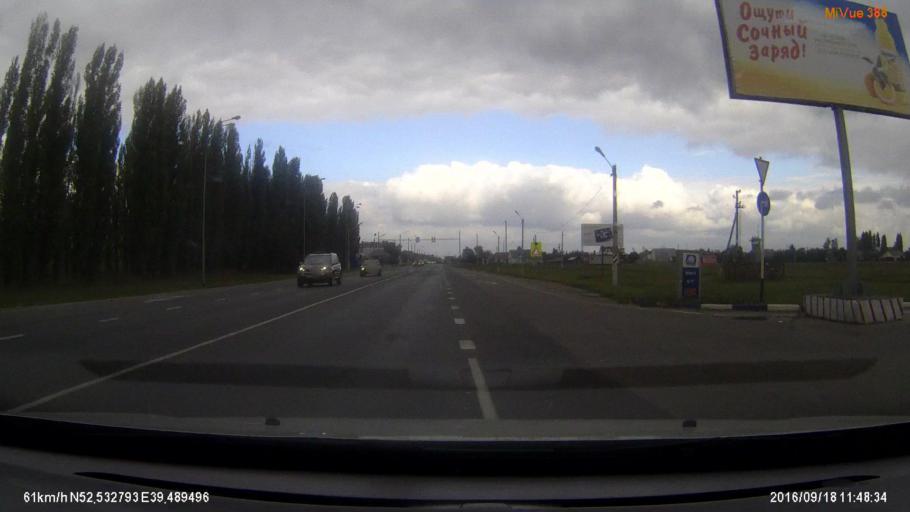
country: RU
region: Lipetsk
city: Syrskoye
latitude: 52.5325
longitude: 39.4892
